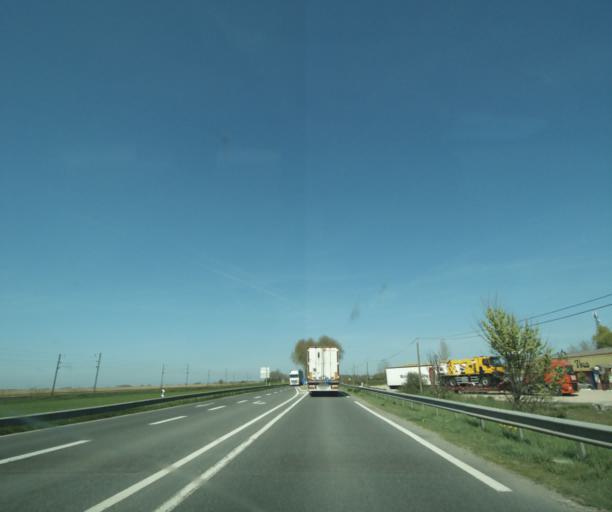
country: FR
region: Bourgogne
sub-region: Departement de la Nievre
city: Chantenay-Saint-Imbert
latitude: 46.7033
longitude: 3.2016
